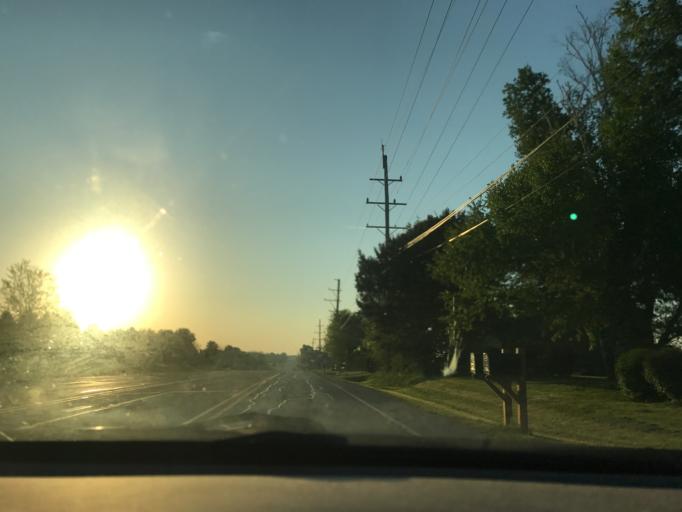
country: US
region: Illinois
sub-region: Kane County
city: South Elgin
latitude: 42.0067
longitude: -88.3595
